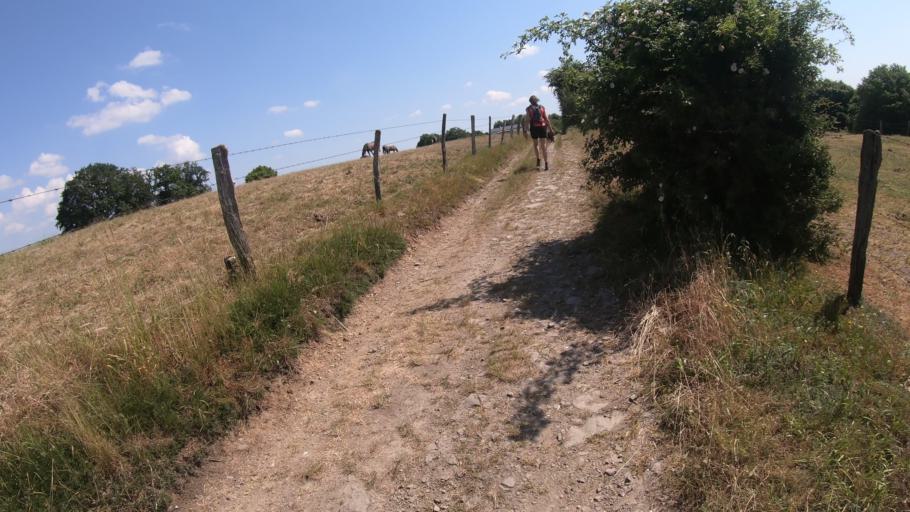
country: BE
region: Wallonia
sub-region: Province de Liege
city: Trooz
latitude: 50.5694
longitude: 5.7104
